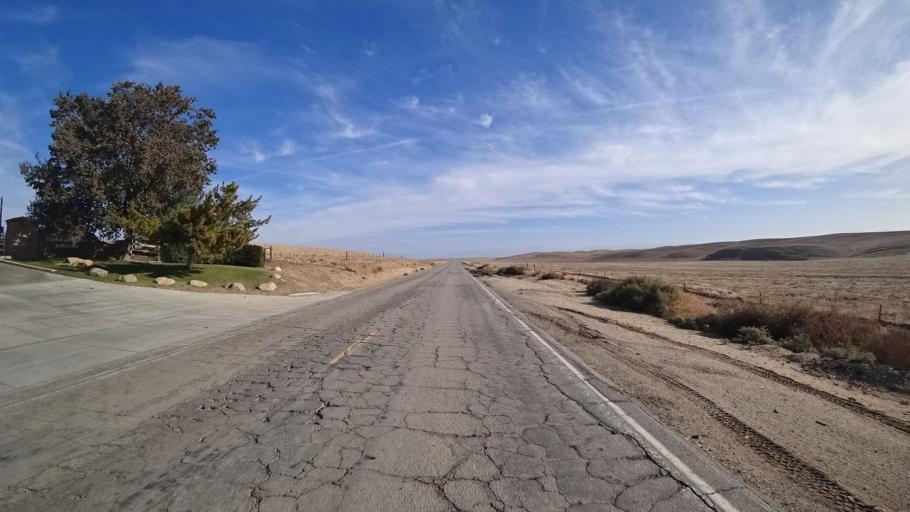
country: US
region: California
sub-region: Kern County
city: McFarland
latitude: 35.6052
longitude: -119.0677
